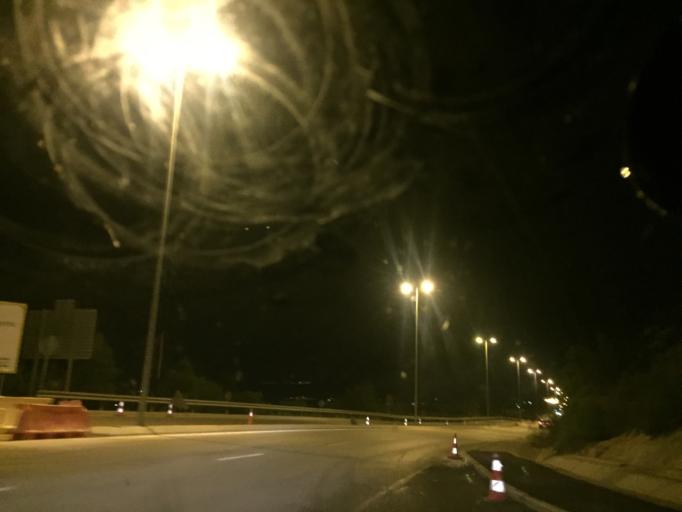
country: ES
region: Andalusia
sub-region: Provincia de Jaen
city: Jaen
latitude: 37.7824
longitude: -3.8229
